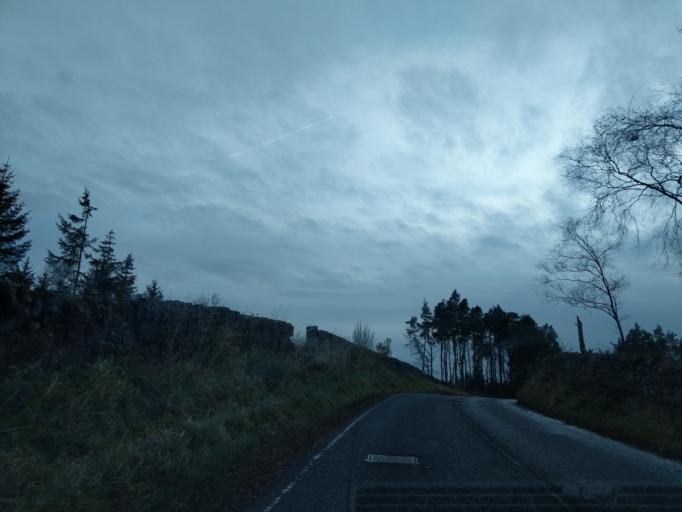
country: GB
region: Scotland
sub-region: West Lothian
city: Linlithgow
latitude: 55.9516
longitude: -3.6110
